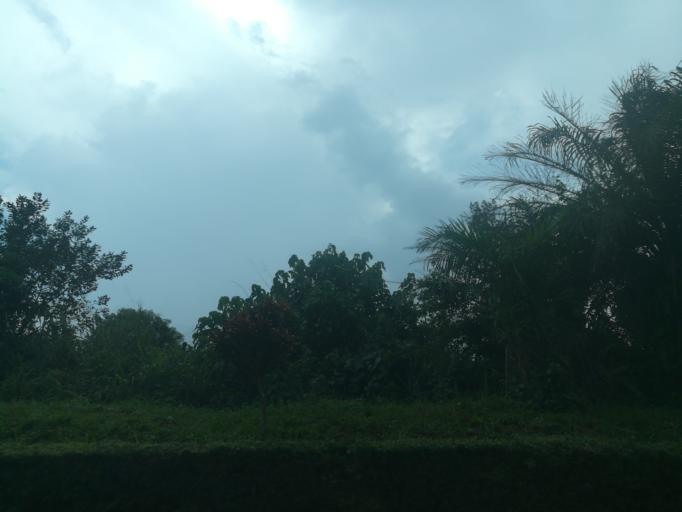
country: NG
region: Lagos
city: Ikorodu
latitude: 6.6399
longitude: 3.5211
